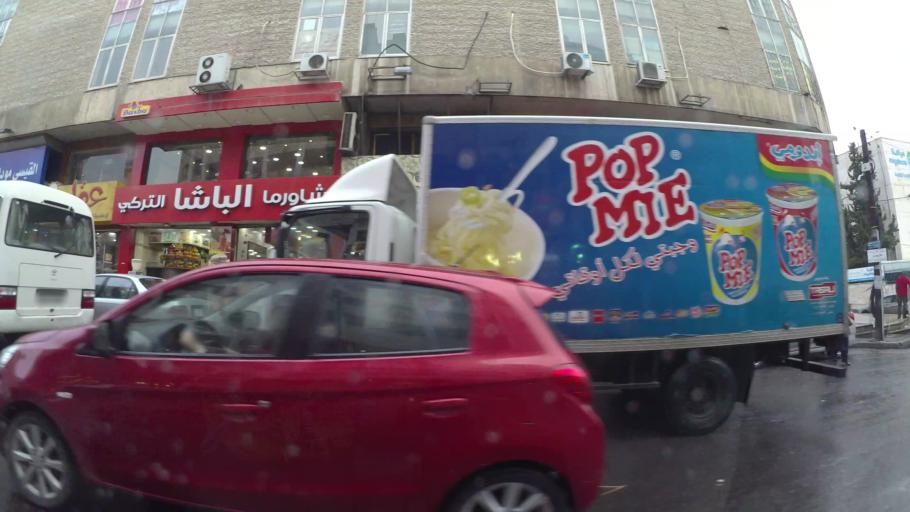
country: JO
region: Amman
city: Amman
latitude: 31.9690
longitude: 35.9193
